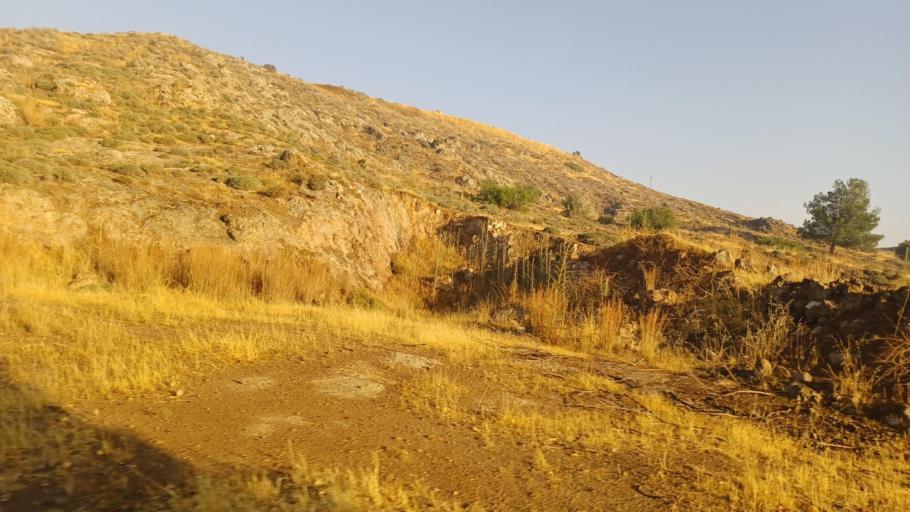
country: CY
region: Larnaka
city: Mosfiloti
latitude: 34.9757
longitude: 33.4342
